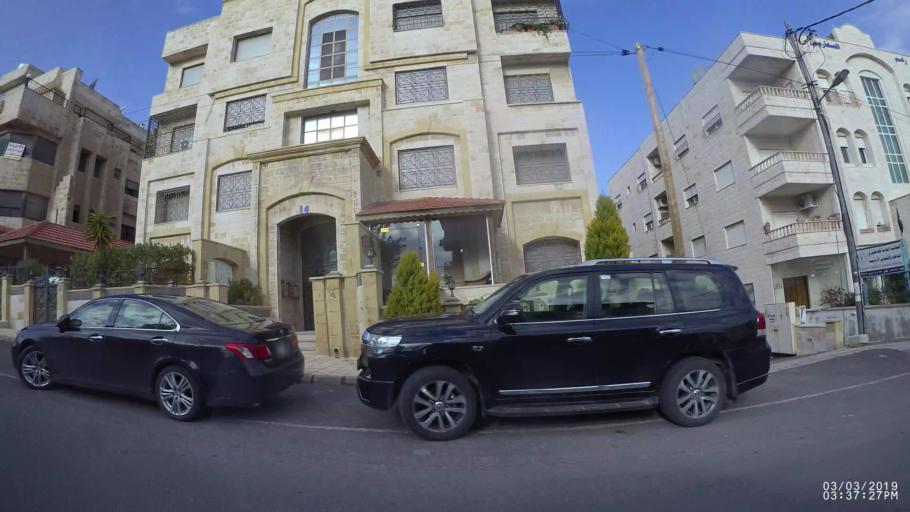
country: JO
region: Amman
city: Al Jubayhah
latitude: 31.9778
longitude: 35.8861
